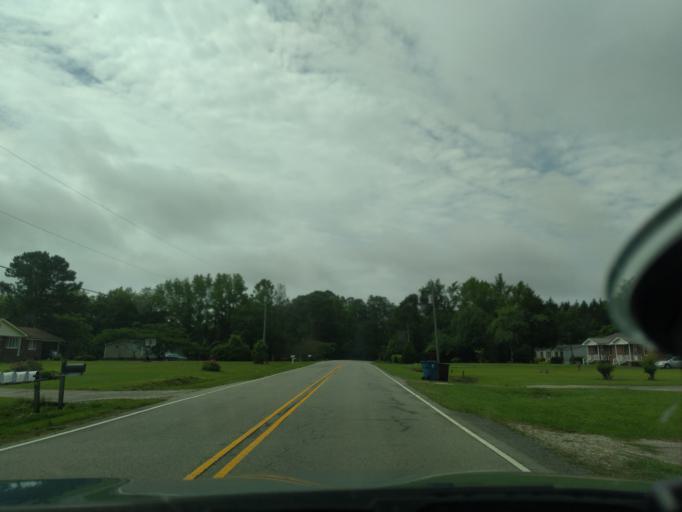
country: US
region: North Carolina
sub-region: Chowan County
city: Edenton
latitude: 35.9096
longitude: -76.6029
